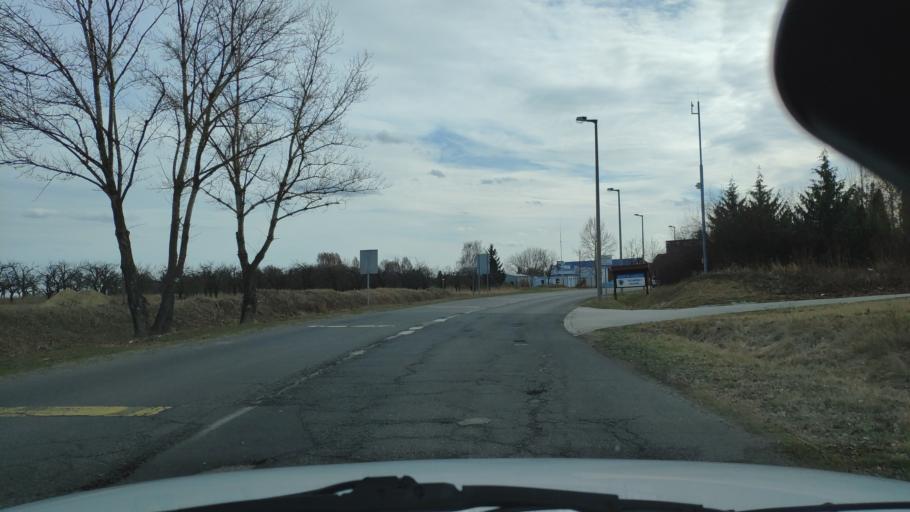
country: HU
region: Bacs-Kiskun
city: Lajosmizse
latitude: 47.0360
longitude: 19.5657
